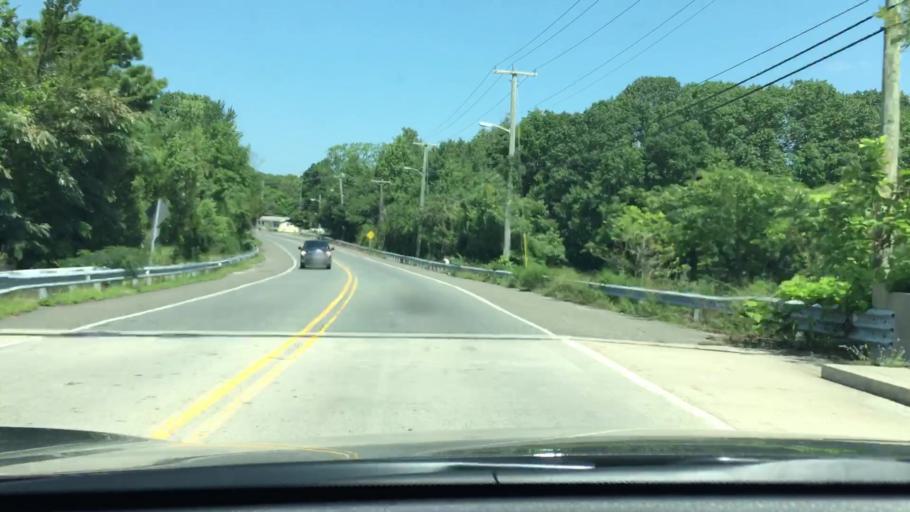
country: US
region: New Jersey
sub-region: Cumberland County
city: Laurel Lake
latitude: 39.3326
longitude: -75.0198
